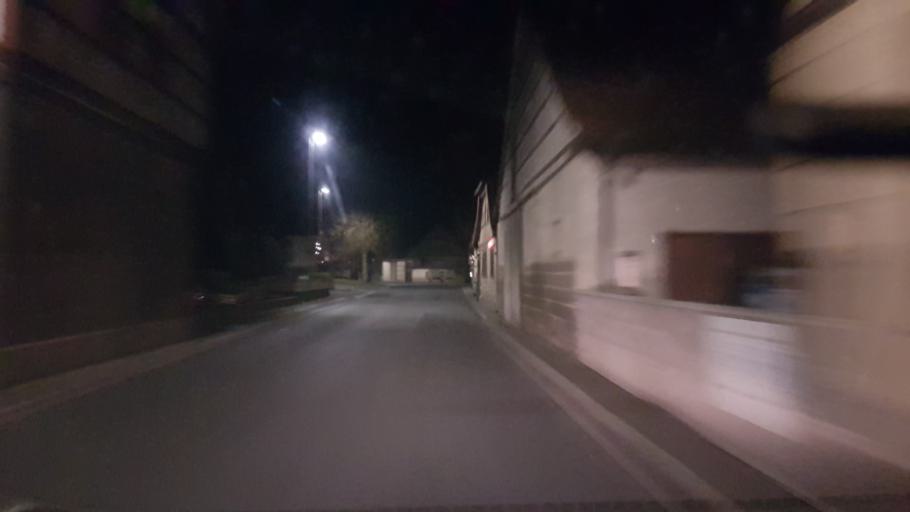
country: DE
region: Bavaria
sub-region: Regierungsbezirk Unterfranken
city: Pfarrweisach
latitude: 50.1613
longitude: 10.7280
